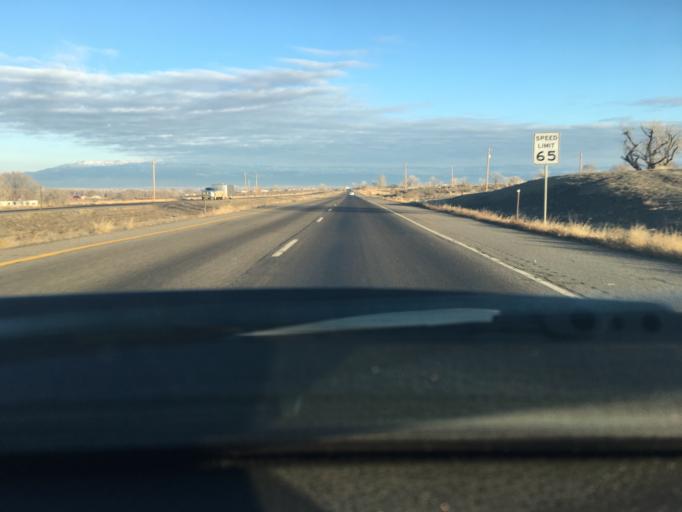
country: US
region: Colorado
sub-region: Montrose County
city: Olathe
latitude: 38.6222
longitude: -107.9848
